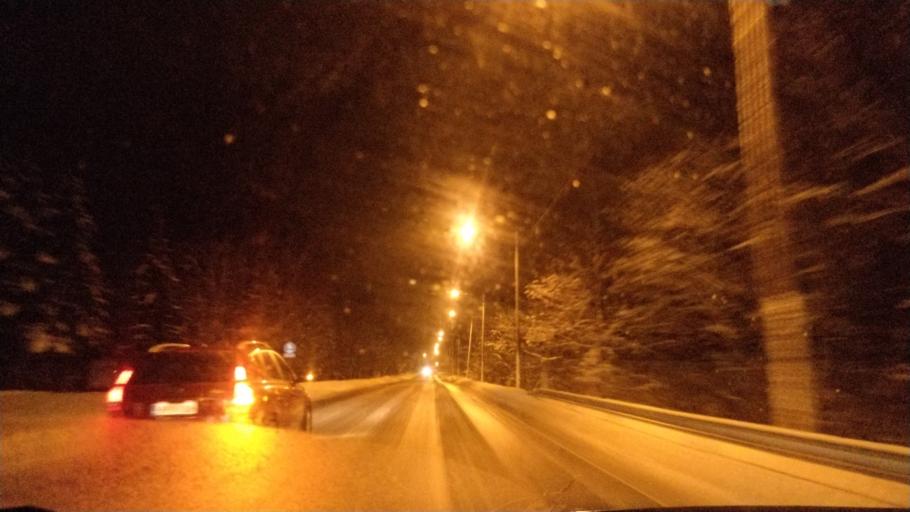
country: FI
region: Lapland
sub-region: Rovaniemi
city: Rovaniemi
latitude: 66.2660
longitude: 25.3348
